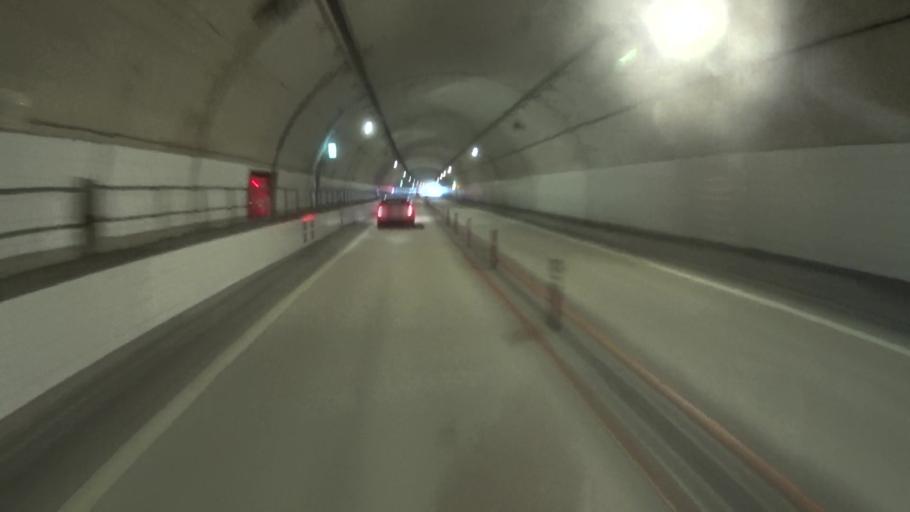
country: JP
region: Kyoto
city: Miyazu
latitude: 35.5229
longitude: 135.1815
